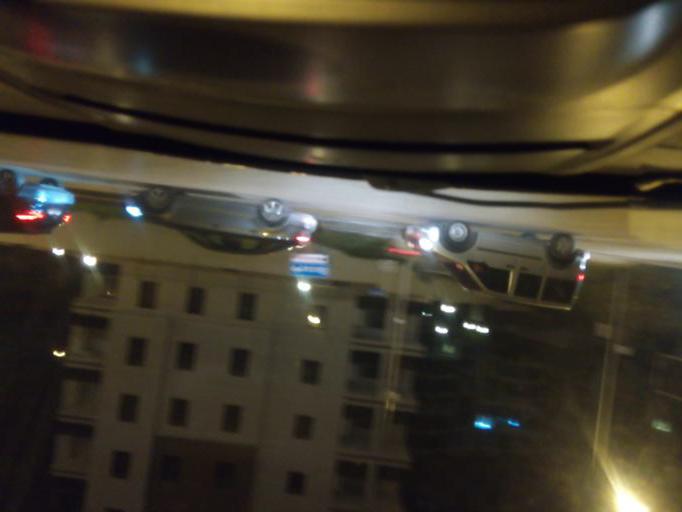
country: TR
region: Bursa
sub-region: Mudanya
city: Mudanya
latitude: 40.3543
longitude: 28.9189
